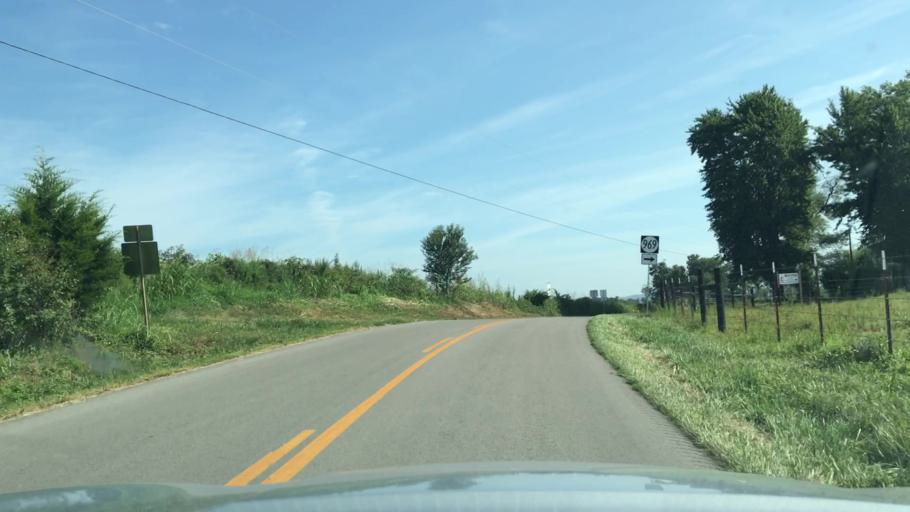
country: US
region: Tennessee
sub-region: Pickett County
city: Byrdstown
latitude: 36.6346
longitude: -85.0858
